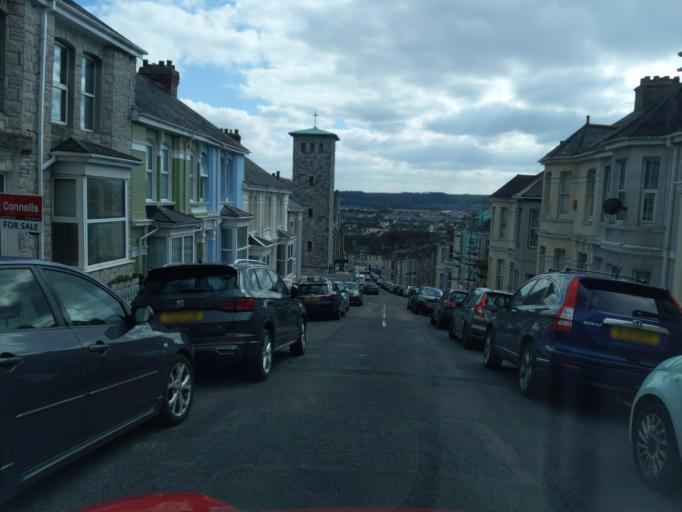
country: GB
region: England
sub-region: Plymouth
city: Plymouth
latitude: 50.3770
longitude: -4.1212
